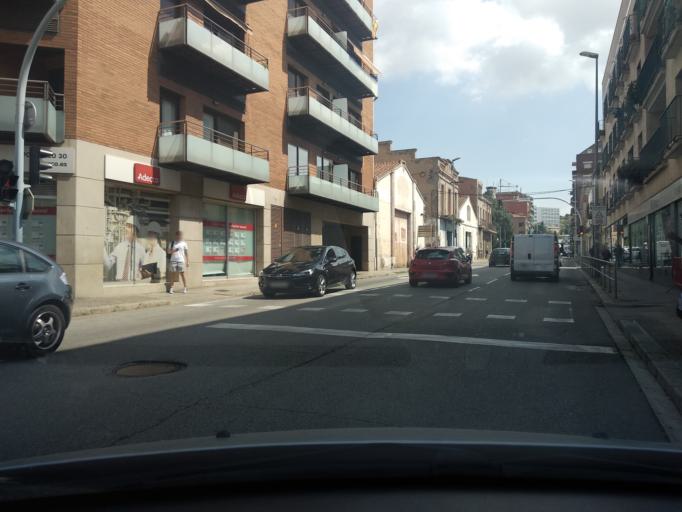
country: ES
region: Catalonia
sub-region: Provincia de Barcelona
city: Granollers
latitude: 41.6137
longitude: 2.2905
